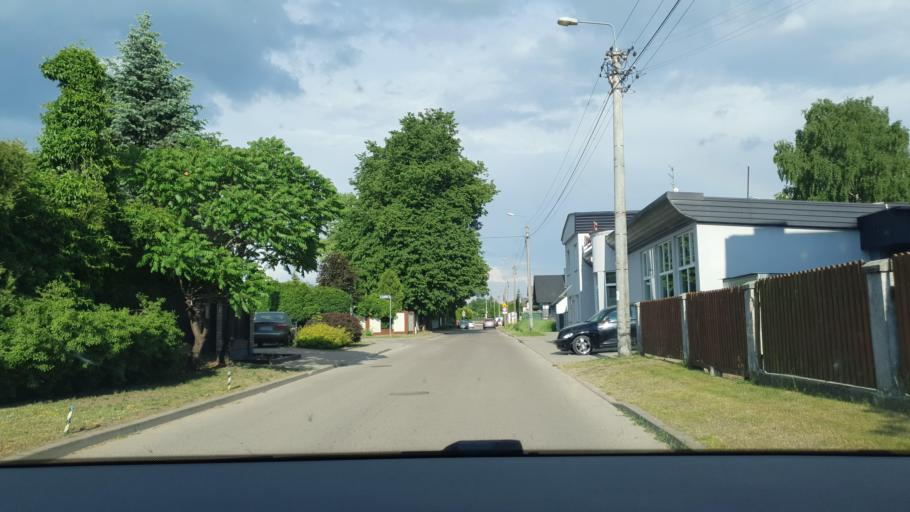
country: PL
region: Podlasie
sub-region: Powiat bialostocki
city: Wasilkow
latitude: 53.1275
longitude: 23.2541
